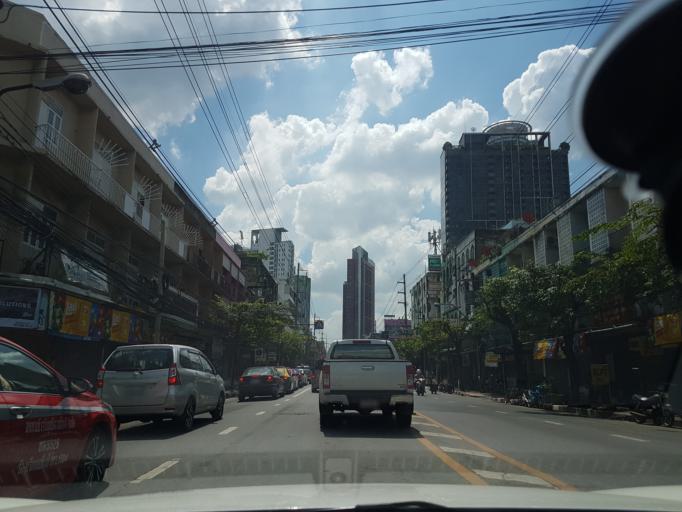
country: TH
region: Bangkok
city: Phra Khanong
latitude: 13.7169
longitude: 100.5955
